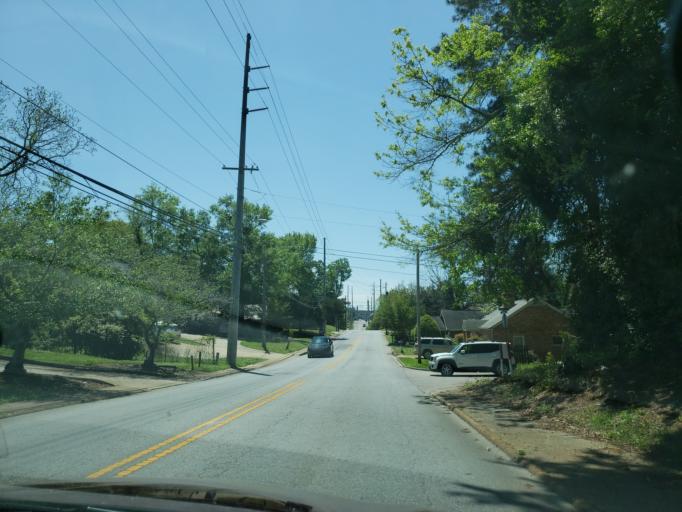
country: US
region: Alabama
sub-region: Lee County
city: Auburn
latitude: 32.6152
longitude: -85.4904
